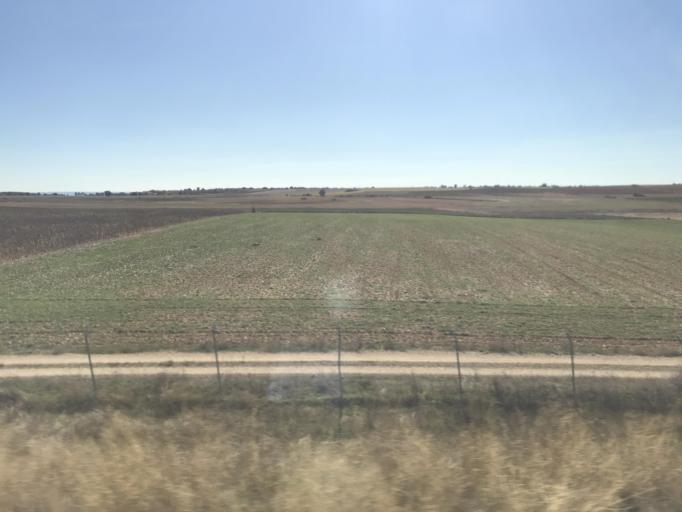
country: ES
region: Castille-La Mancha
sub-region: Provincia de Guadalajara
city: Almadrones
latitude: 40.8678
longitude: -2.7798
